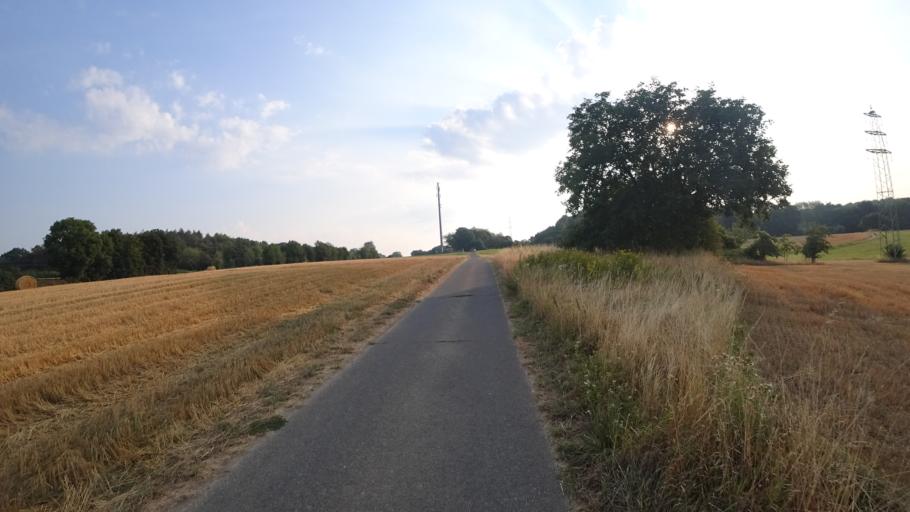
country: DE
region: Rheinland-Pfalz
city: Weitersburg
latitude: 50.4258
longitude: 7.6244
